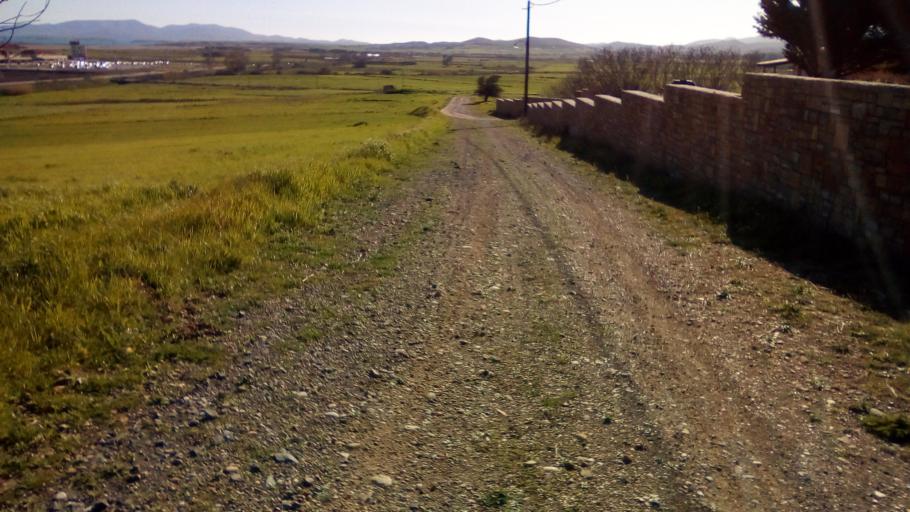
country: GR
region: North Aegean
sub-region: Nomos Lesvou
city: Myrina
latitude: 39.9304
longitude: 25.2350
